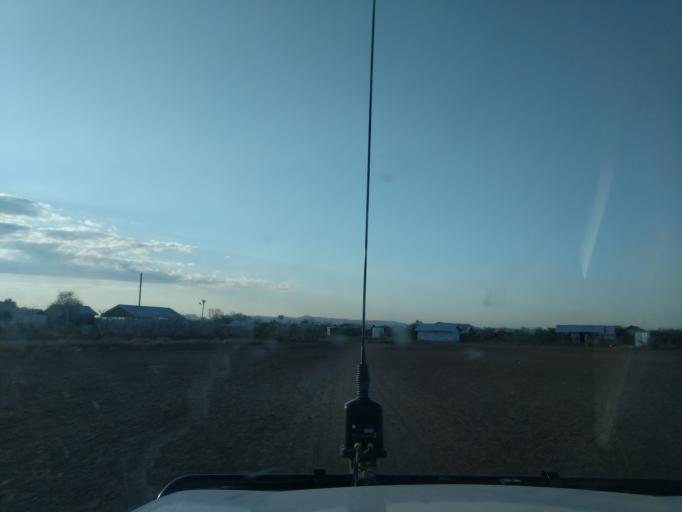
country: UG
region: Northern Region
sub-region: Kaabong District
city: Kaabong
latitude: 3.7576
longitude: 34.8098
